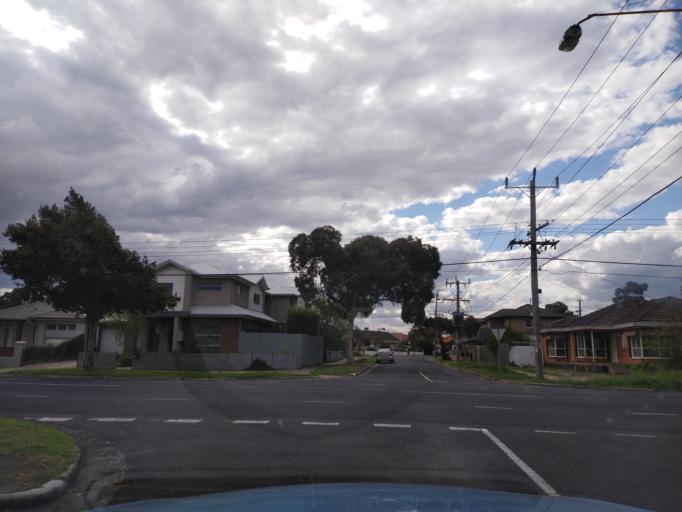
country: AU
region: Victoria
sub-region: Hobsons Bay
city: Altona North
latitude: -37.8443
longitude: 144.8500
